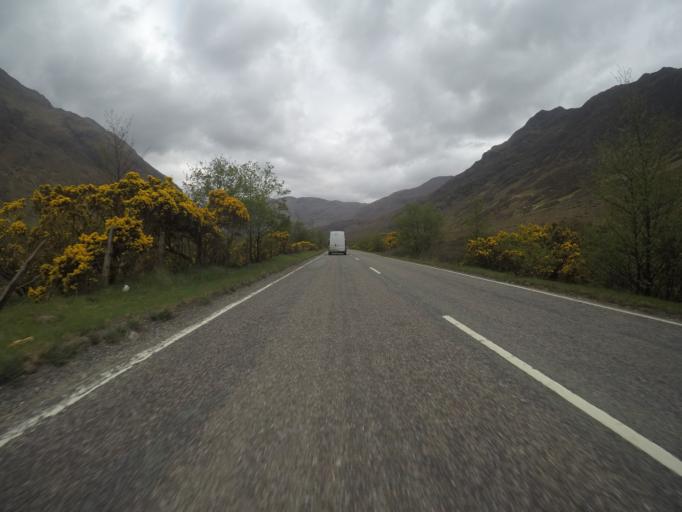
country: GB
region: Scotland
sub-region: Highland
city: Fort William
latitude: 57.1897
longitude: -5.3851
